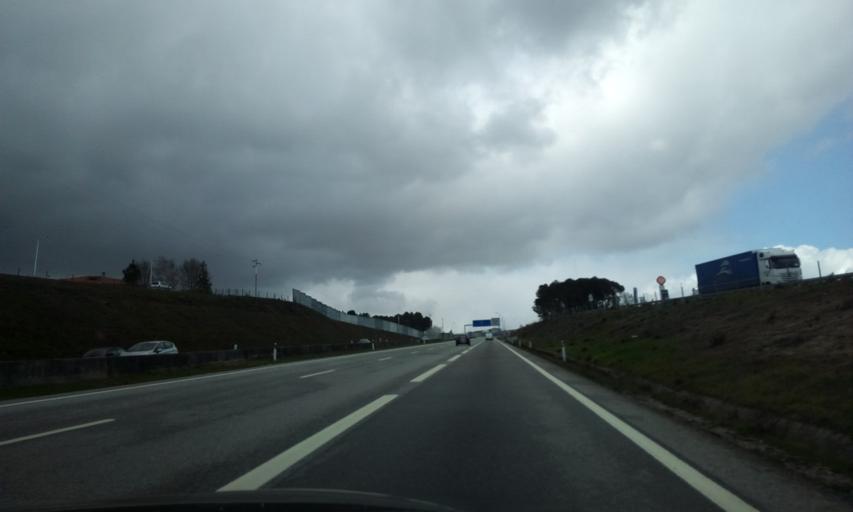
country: PT
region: Viseu
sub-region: Viseu
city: Rio de Loba
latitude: 40.6332
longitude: -7.8446
